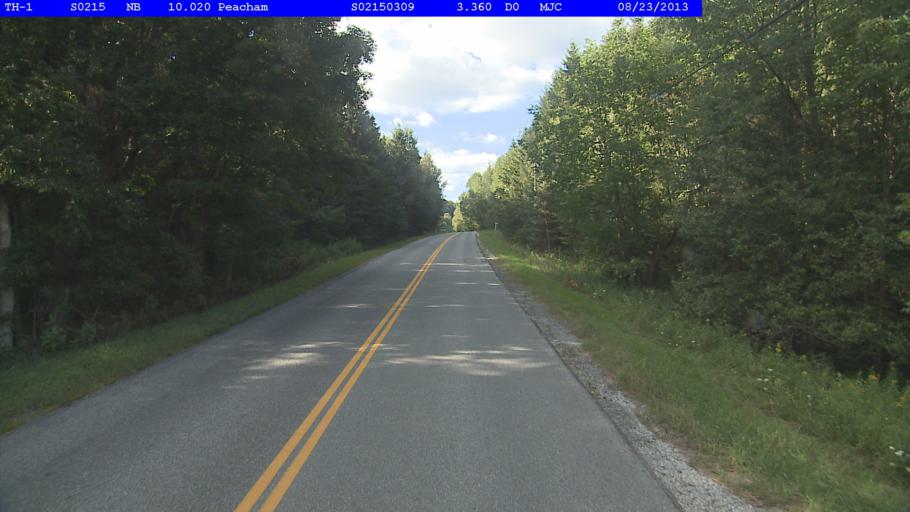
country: US
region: Vermont
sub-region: Caledonia County
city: Saint Johnsbury
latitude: 44.3448
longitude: -72.1766
